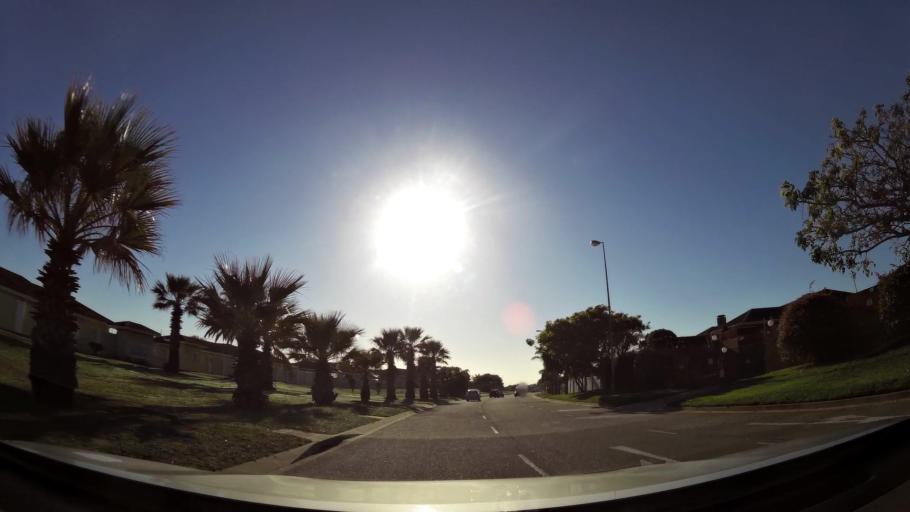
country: ZA
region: Eastern Cape
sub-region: Nelson Mandela Bay Metropolitan Municipality
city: Port Elizabeth
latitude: -33.9911
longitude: 25.6490
